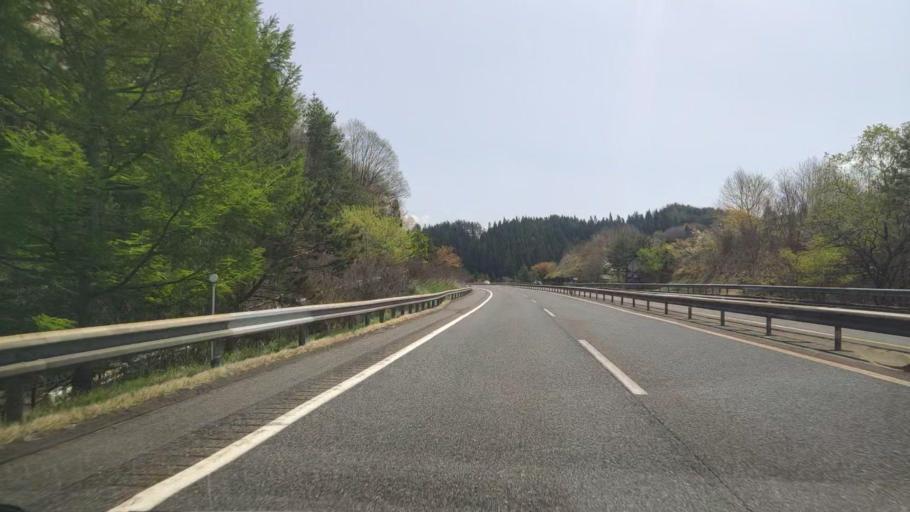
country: JP
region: Iwate
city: Ichinohe
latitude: 40.2039
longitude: 141.1973
